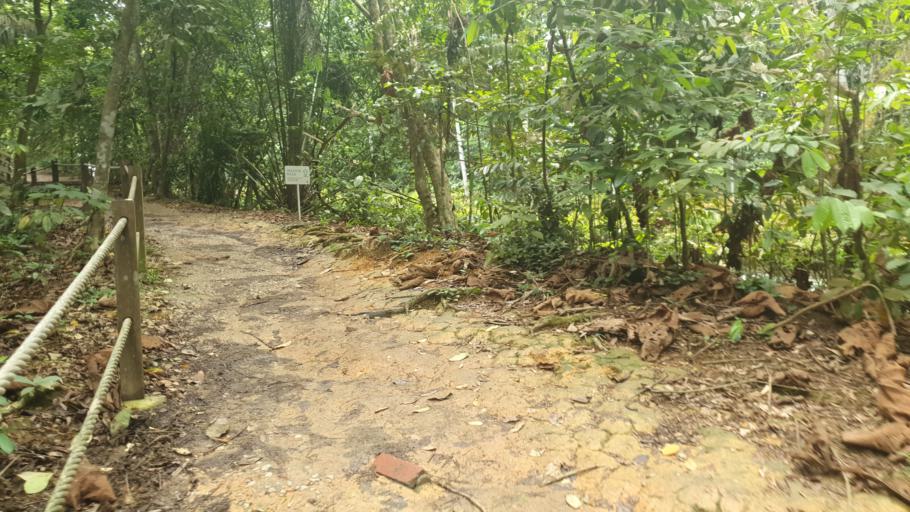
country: SG
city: Singapore
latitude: 1.3606
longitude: 103.8211
